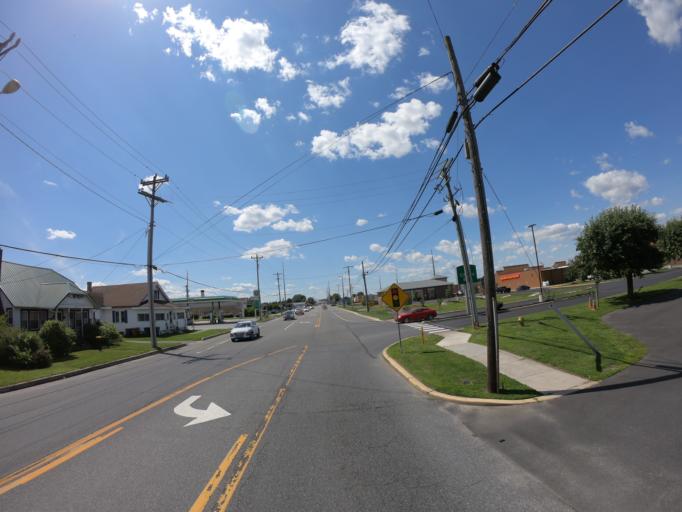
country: US
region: Delaware
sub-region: Sussex County
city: Milford
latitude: 38.9148
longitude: -75.4405
